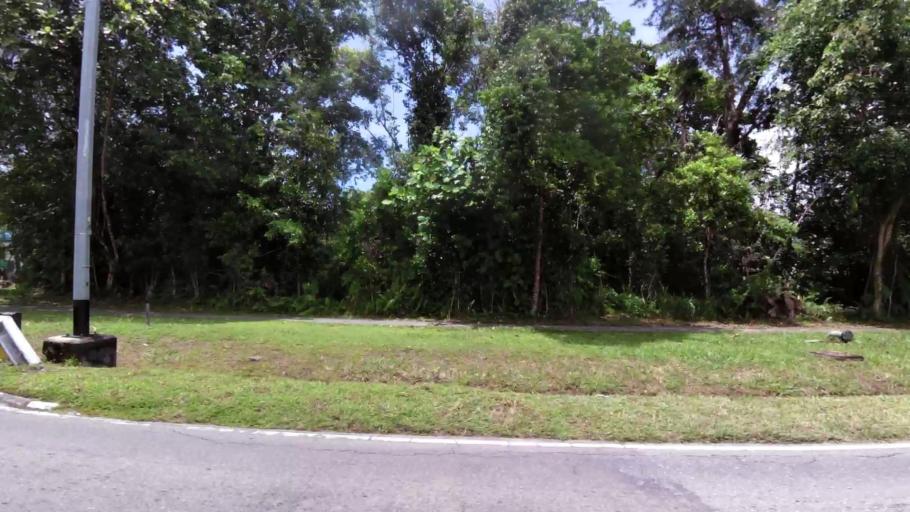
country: BN
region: Belait
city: Kuala Belait
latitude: 4.5997
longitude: 114.2706
